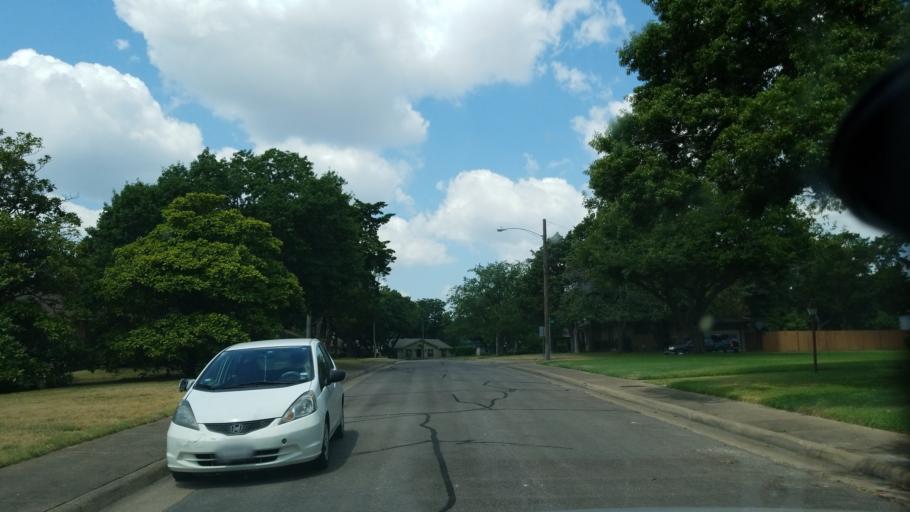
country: US
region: Texas
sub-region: Dallas County
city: Cockrell Hill
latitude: 32.6932
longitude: -96.8842
